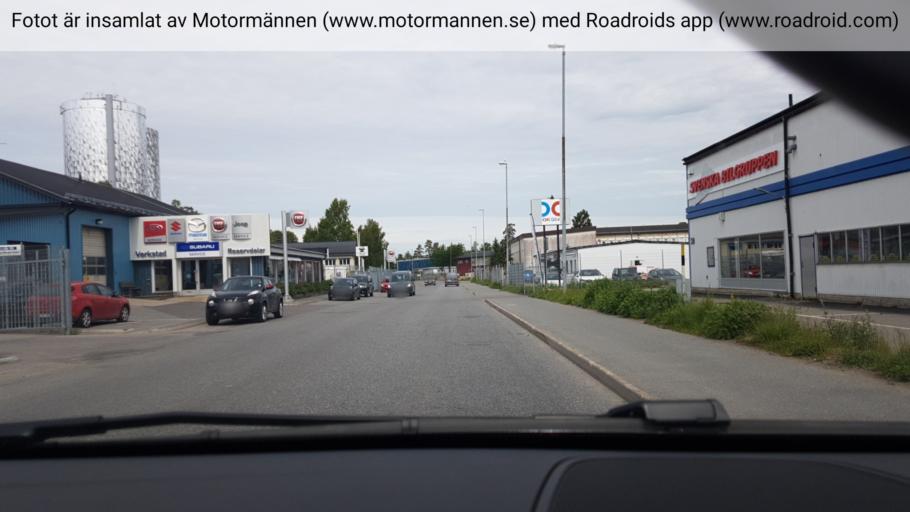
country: SE
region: Stockholm
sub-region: Haninge Kommun
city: Haninge
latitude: 59.1681
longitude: 18.1554
